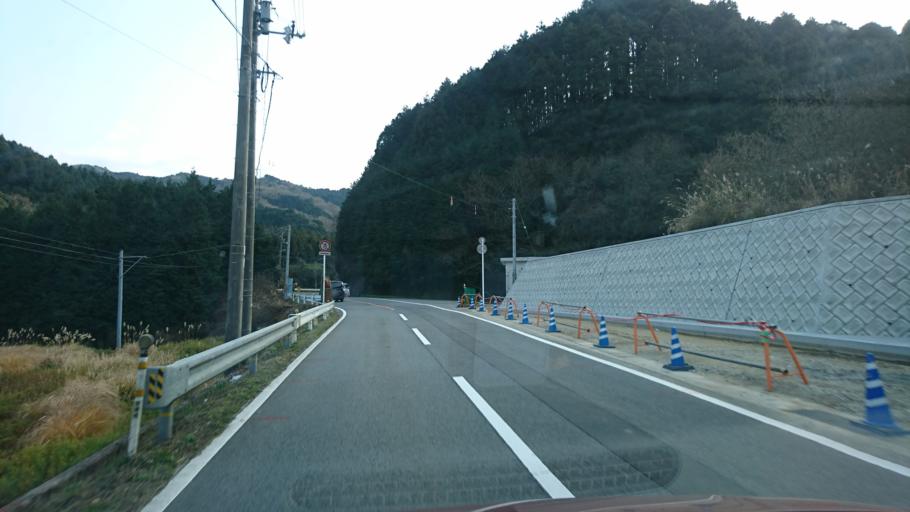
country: JP
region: Ehime
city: Hojo
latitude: 33.9852
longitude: 132.9083
